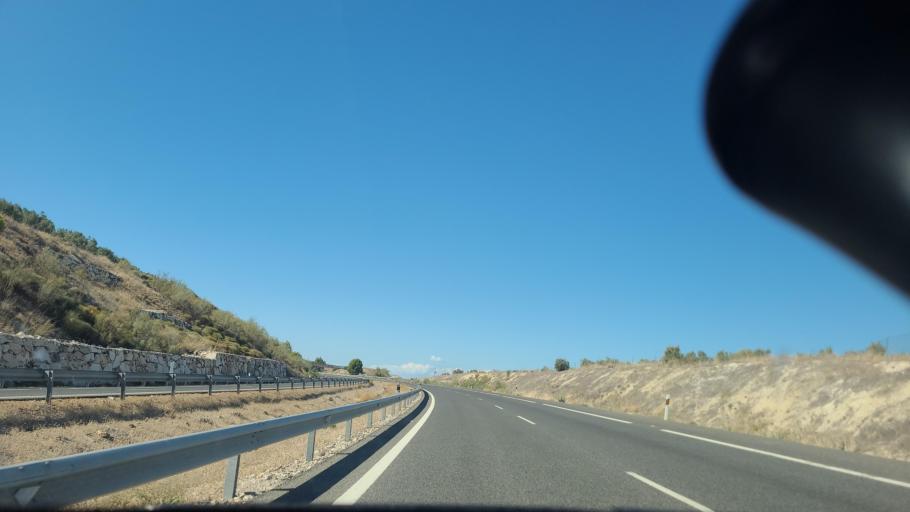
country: ES
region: Andalusia
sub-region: Provincia de Jaen
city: La Guardia de Jaen
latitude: 37.7487
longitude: -3.6883
